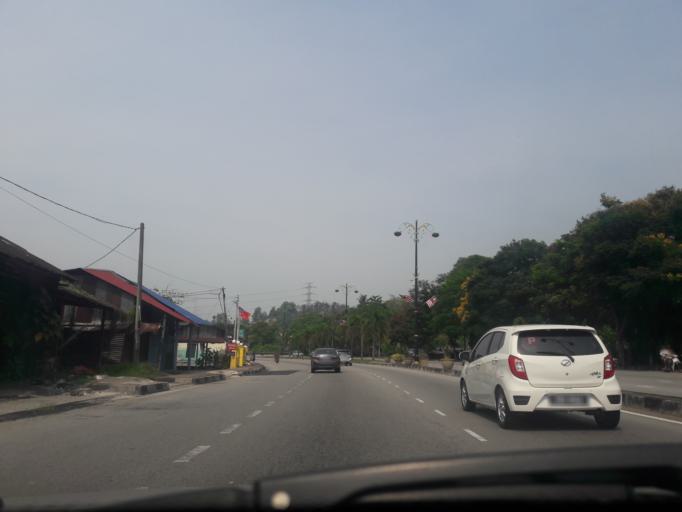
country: MY
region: Kedah
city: Kulim
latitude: 5.3820
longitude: 100.5541
